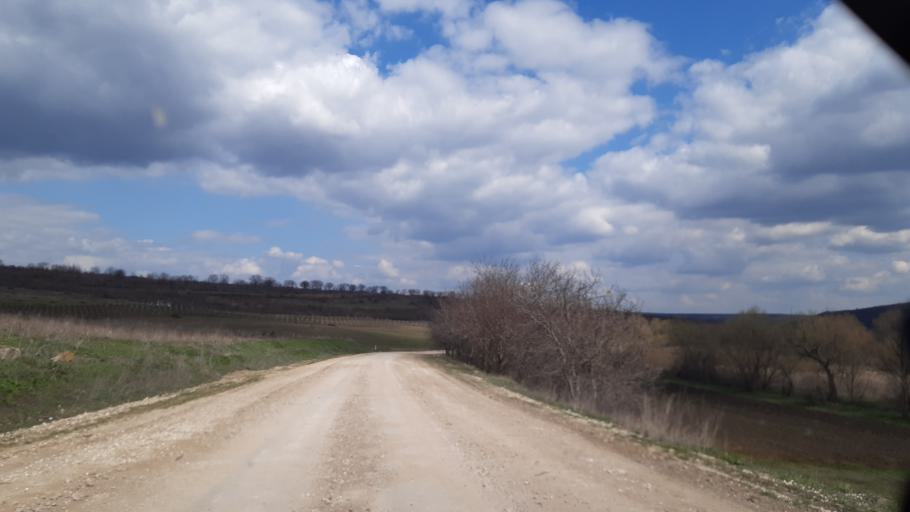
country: MD
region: Laloveni
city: Ialoveni
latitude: 46.8891
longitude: 28.7007
